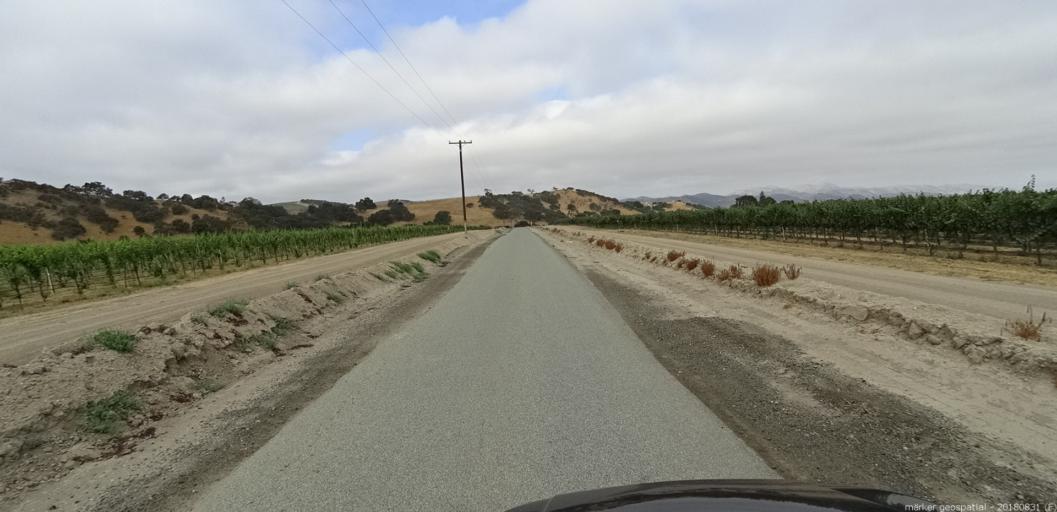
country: US
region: California
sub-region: Monterey County
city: King City
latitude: 36.1399
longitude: -121.0958
